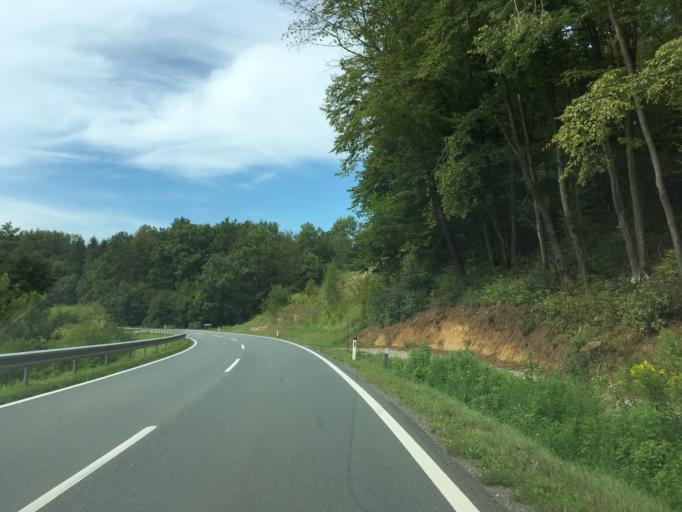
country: AT
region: Styria
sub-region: Politischer Bezirk Deutschlandsberg
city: Wettmannstatten
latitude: 46.8044
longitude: 15.3914
